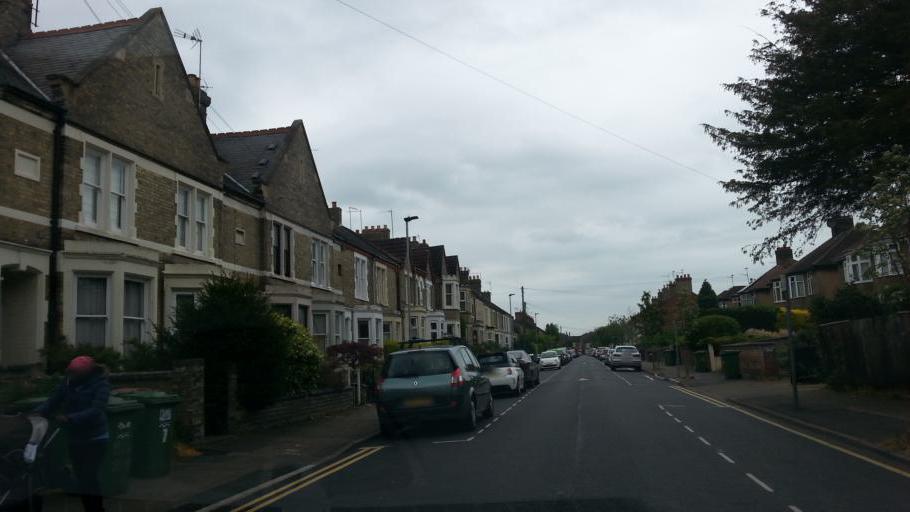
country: GB
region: England
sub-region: Peterborough
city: Peterborough
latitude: 52.5835
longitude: -0.2382
